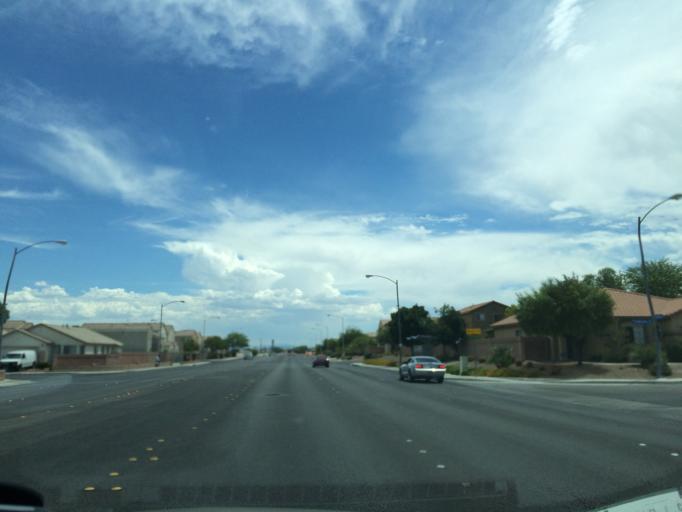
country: US
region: Nevada
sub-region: Clark County
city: North Las Vegas
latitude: 36.2516
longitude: -115.1801
